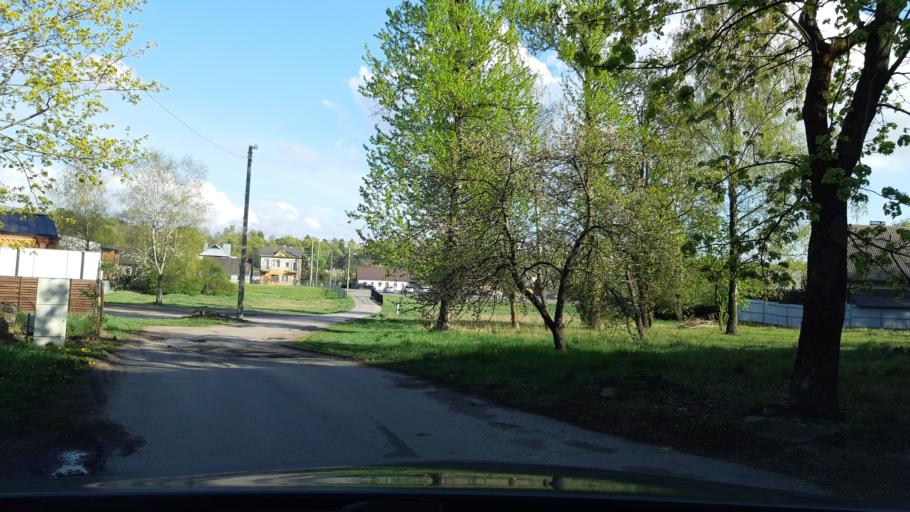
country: LT
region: Kauno apskritis
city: Dainava (Kaunas)
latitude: 54.8671
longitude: 23.9665
